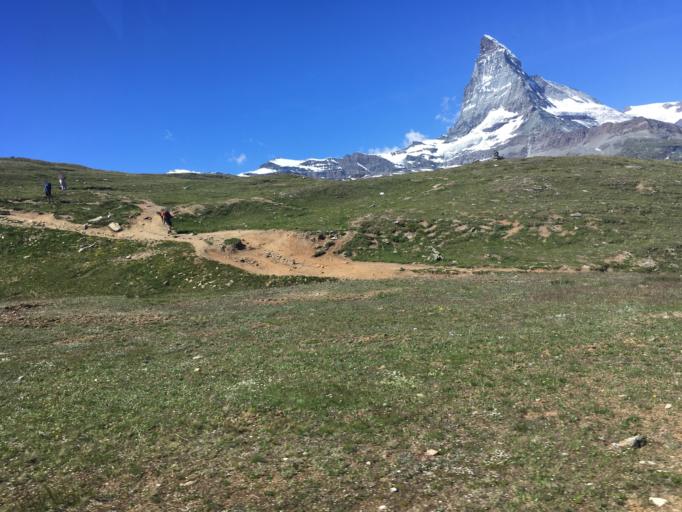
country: CH
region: Valais
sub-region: Visp District
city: Zermatt
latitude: 45.9907
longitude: 7.7558
